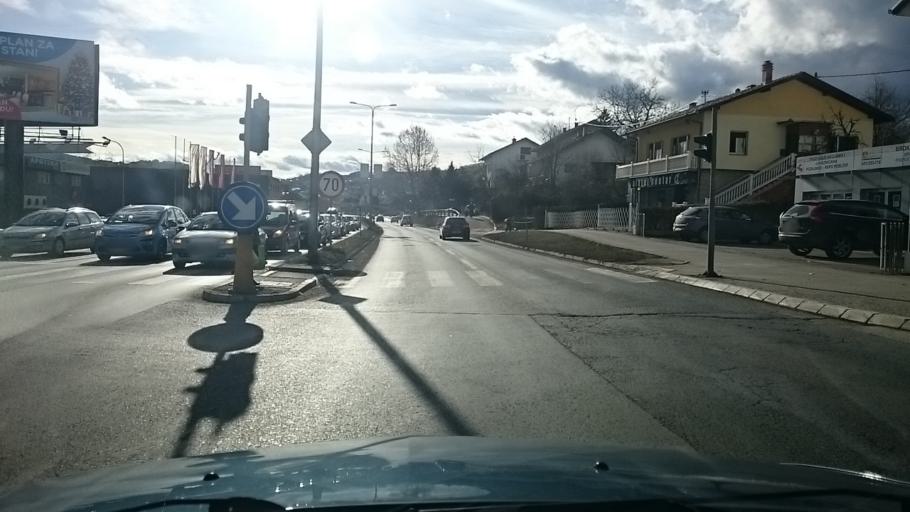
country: BA
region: Republika Srpska
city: Banja Luka
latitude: 44.7781
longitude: 17.1851
